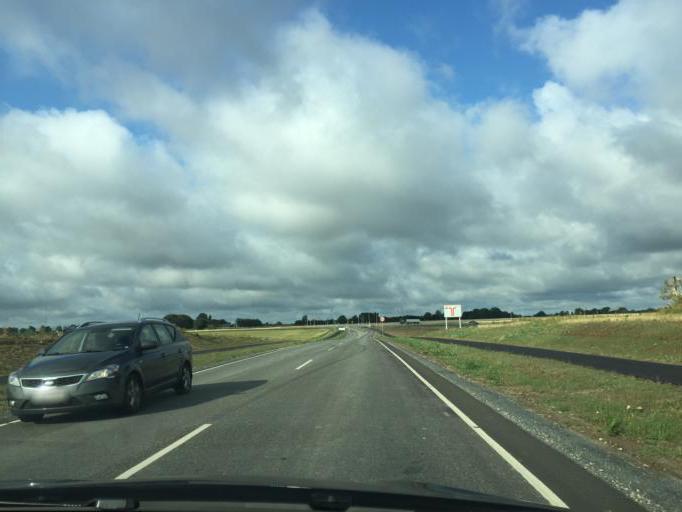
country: DK
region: South Denmark
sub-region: Odense Kommune
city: Hojby
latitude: 55.3418
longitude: 10.3866
